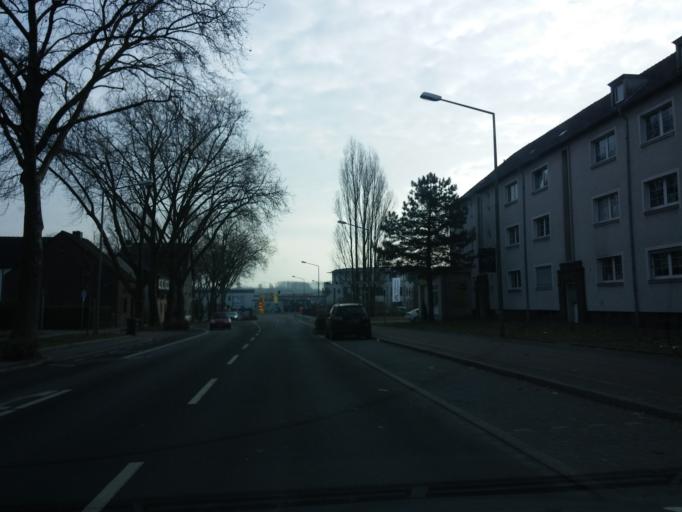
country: DE
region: North Rhine-Westphalia
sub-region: Regierungsbezirk Munster
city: Gladbeck
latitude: 51.5367
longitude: 6.9762
